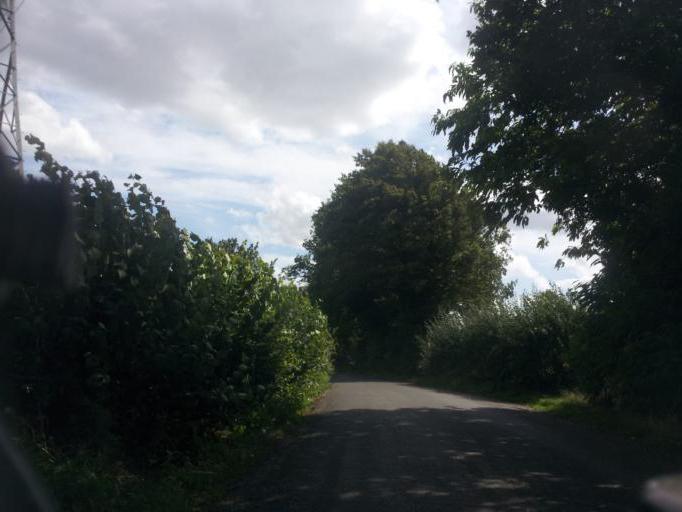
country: GB
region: England
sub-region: Kent
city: Newington
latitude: 51.3642
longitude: 0.6605
